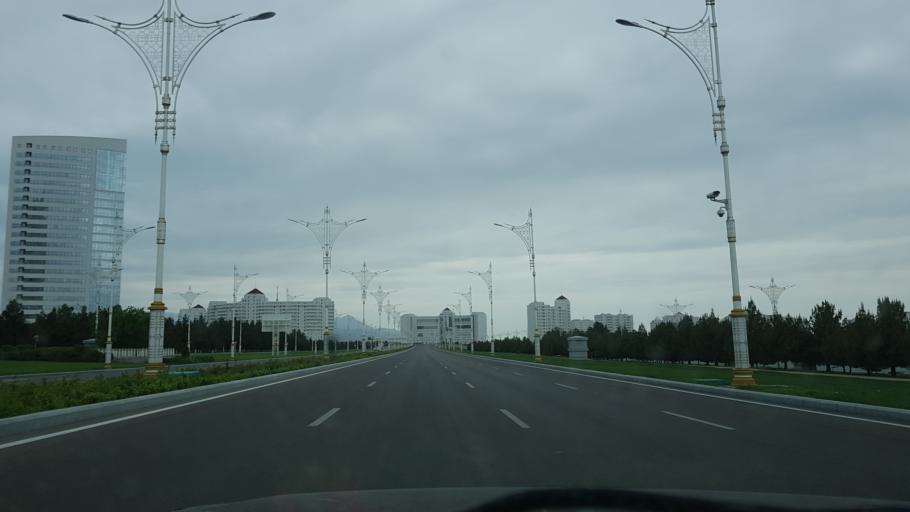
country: TM
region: Ahal
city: Ashgabat
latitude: 37.8906
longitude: 58.3465
